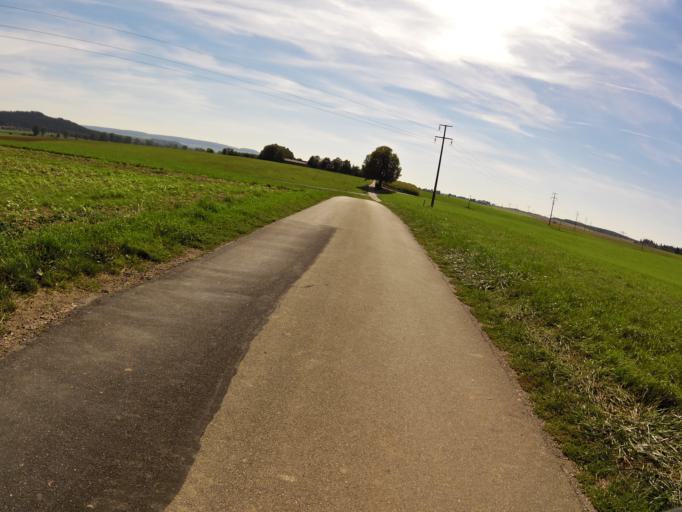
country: DE
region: Baden-Wuerttemberg
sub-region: Freiburg Region
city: Bad Durrheim
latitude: 48.0014
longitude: 8.5025
